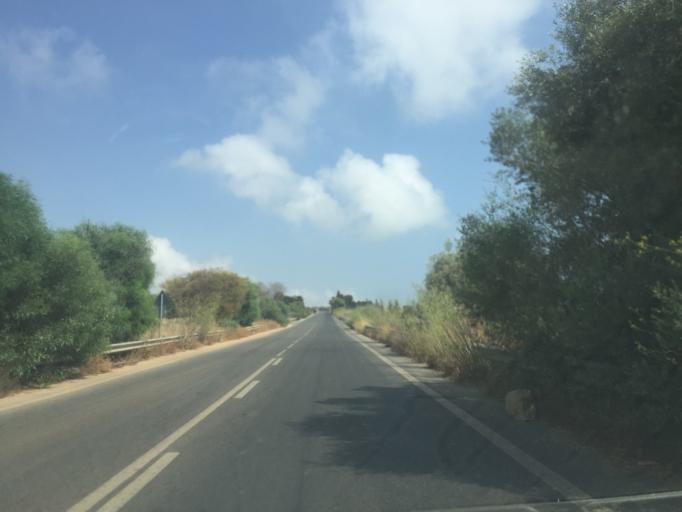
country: IT
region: Sicily
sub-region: Ragusa
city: Donnalucata
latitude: 36.7762
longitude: 14.6147
